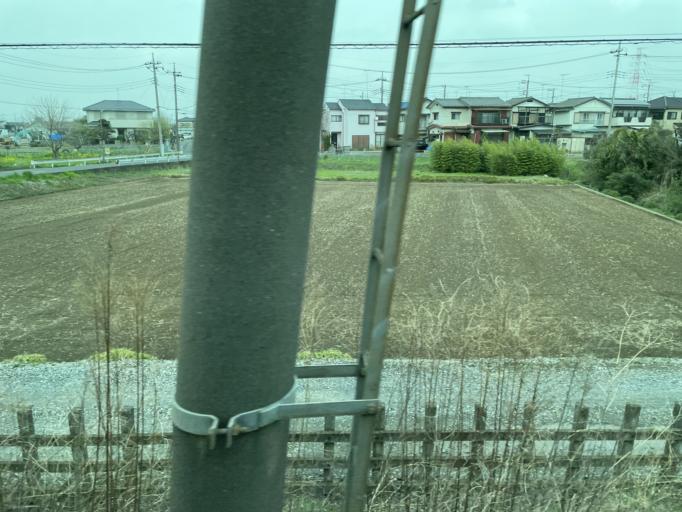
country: JP
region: Saitama
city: Sugito
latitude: 36.0353
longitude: 139.7072
